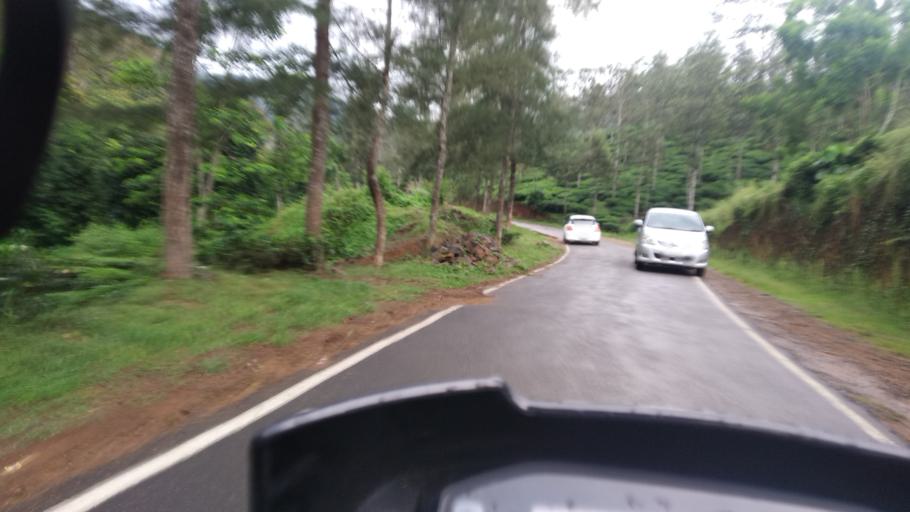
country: IN
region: Tamil Nadu
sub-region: Theni
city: Gudalur
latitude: 9.5673
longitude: 77.0785
